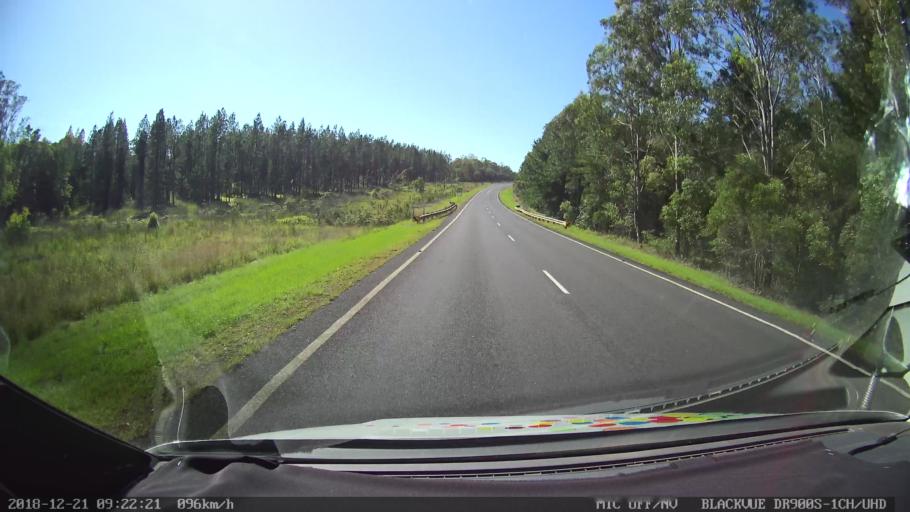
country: AU
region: New South Wales
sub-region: Clarence Valley
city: Maclean
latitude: -29.3408
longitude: 153.0046
